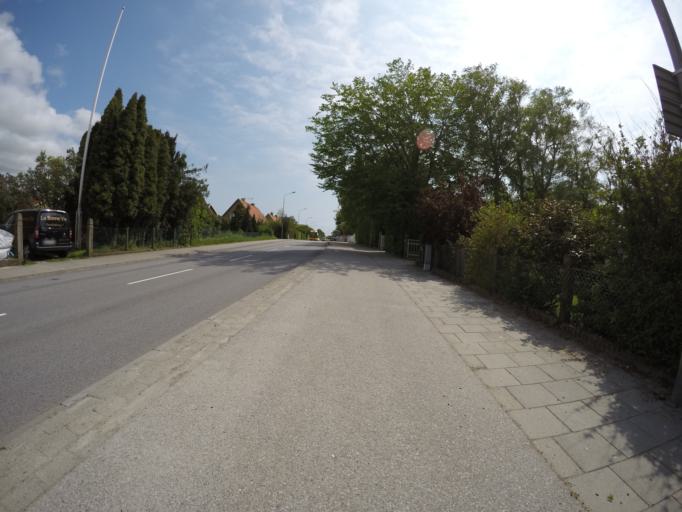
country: SE
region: Skane
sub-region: Malmo
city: Tygelsjo
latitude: 55.5163
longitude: 12.9971
